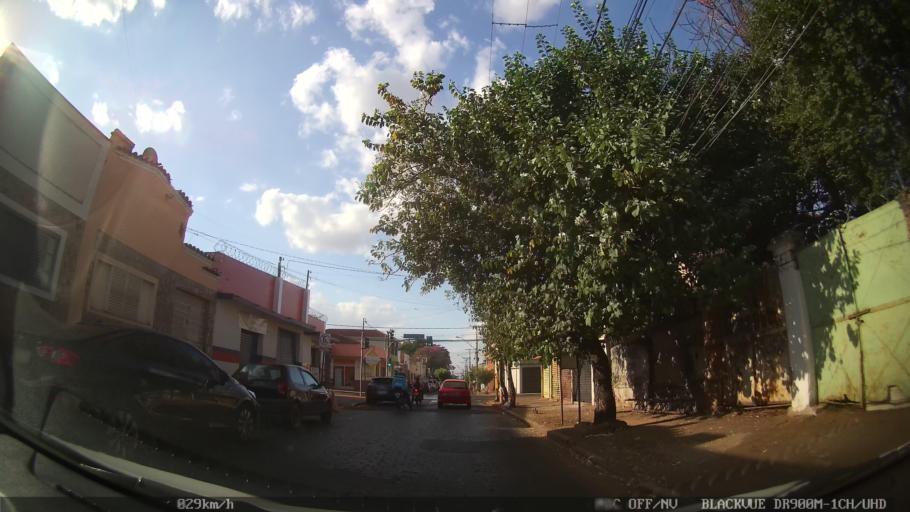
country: BR
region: Sao Paulo
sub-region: Ribeirao Preto
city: Ribeirao Preto
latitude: -21.1707
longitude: -47.8179
